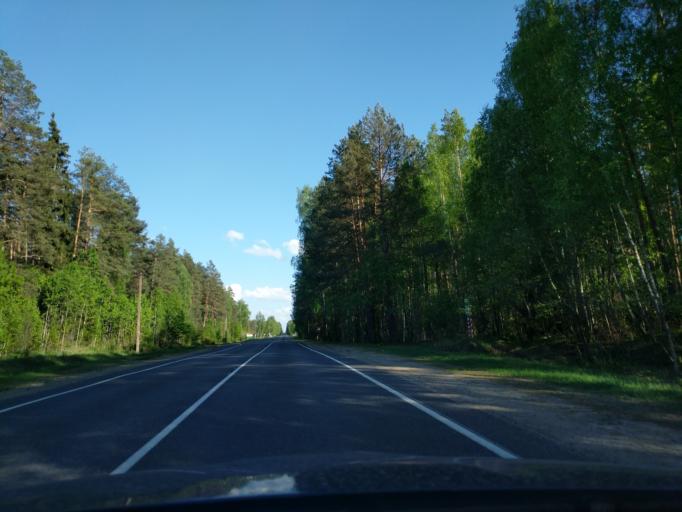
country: BY
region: Minsk
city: Myadzyel
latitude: 54.8174
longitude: 26.9655
